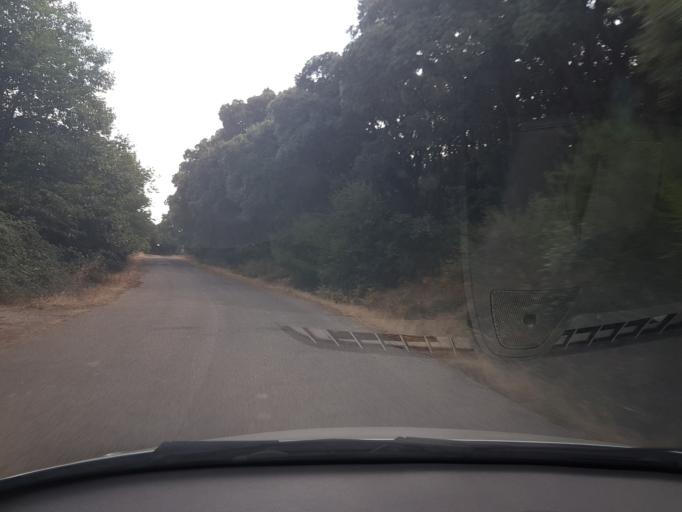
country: IT
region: Sardinia
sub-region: Provincia di Oristano
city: Seneghe
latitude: 40.1114
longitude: 8.6190
